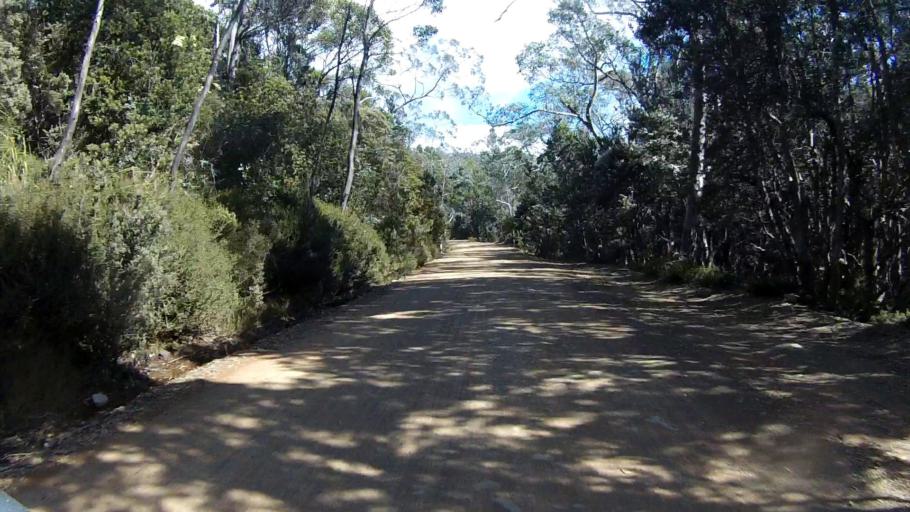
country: AU
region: Tasmania
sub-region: Derwent Valley
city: New Norfolk
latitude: -42.6873
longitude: 146.5961
